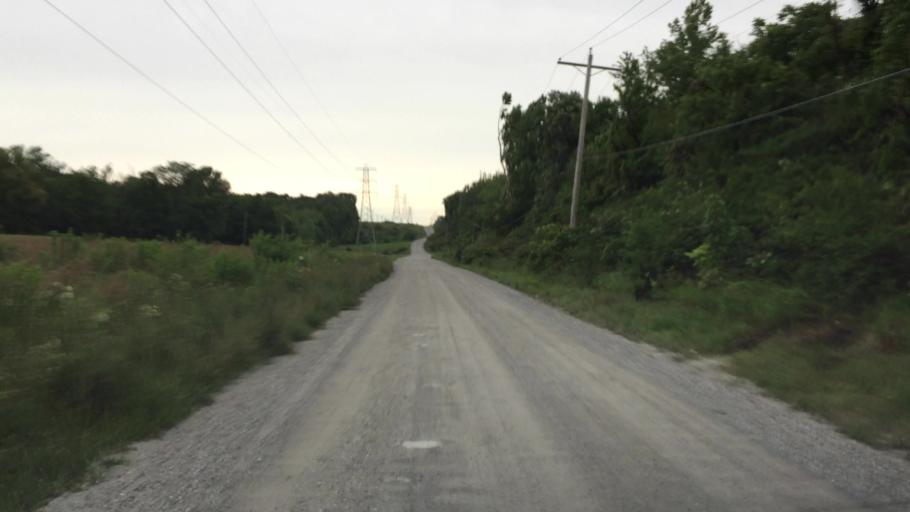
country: US
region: Illinois
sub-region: Hancock County
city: Hamilton
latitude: 40.3637
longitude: -91.3612
